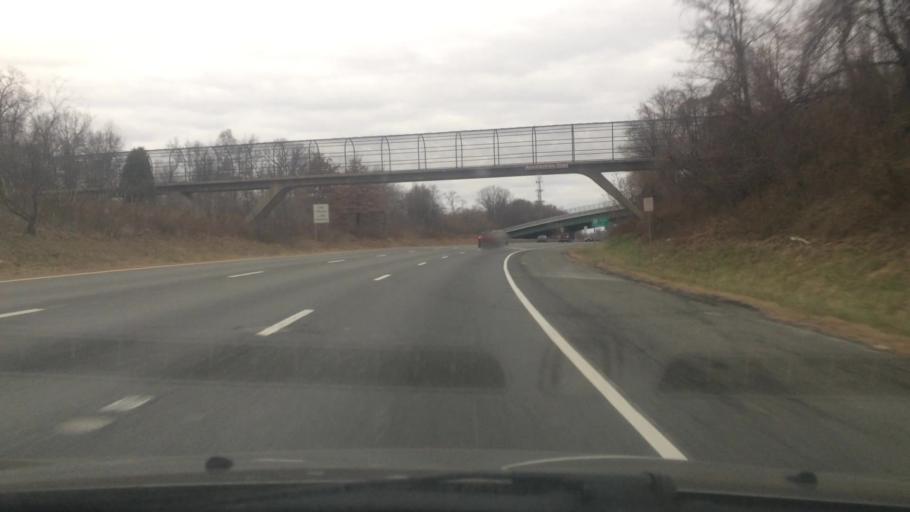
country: US
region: Maryland
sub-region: Frederick County
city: Myersville
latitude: 39.5344
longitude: -77.6060
